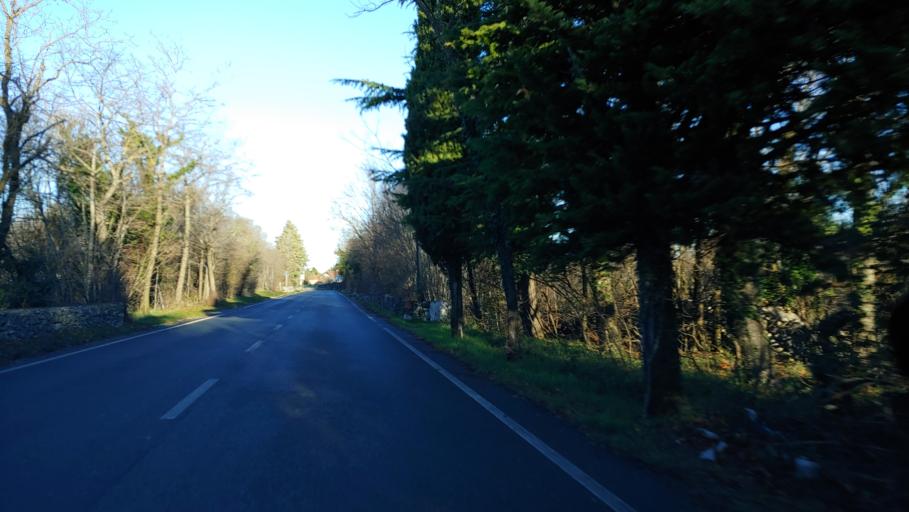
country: IT
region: Friuli Venezia Giulia
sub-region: Provincia di Trieste
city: Villa Opicina
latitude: 45.6677
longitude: 13.8301
